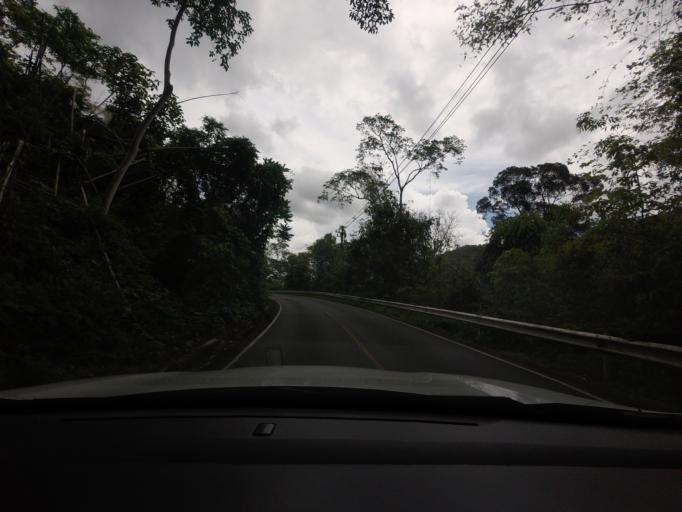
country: TH
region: Nakhon Ratchasima
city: Pak Chong
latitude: 14.4869
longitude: 101.3898
